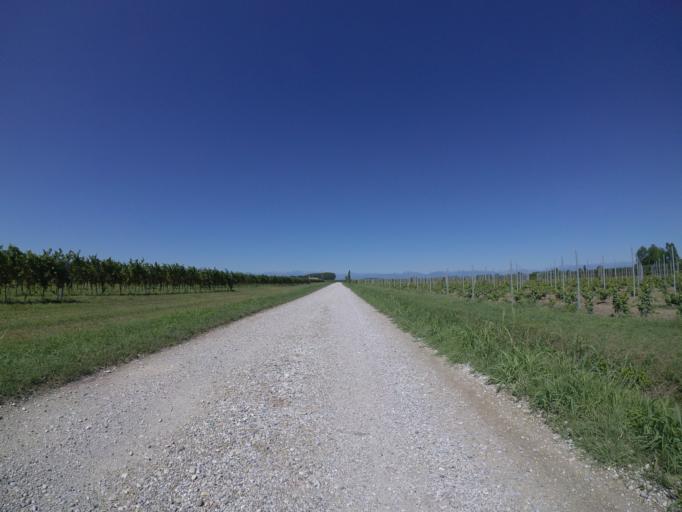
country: IT
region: Friuli Venezia Giulia
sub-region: Provincia di Udine
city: Rivignano
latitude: 45.8632
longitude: 13.0125
